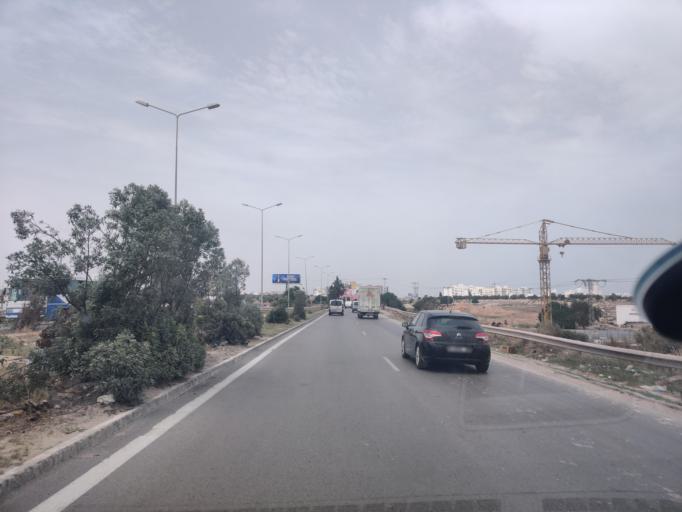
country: TN
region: Susah
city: Hammam Sousse
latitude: 35.8242
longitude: 10.5924
